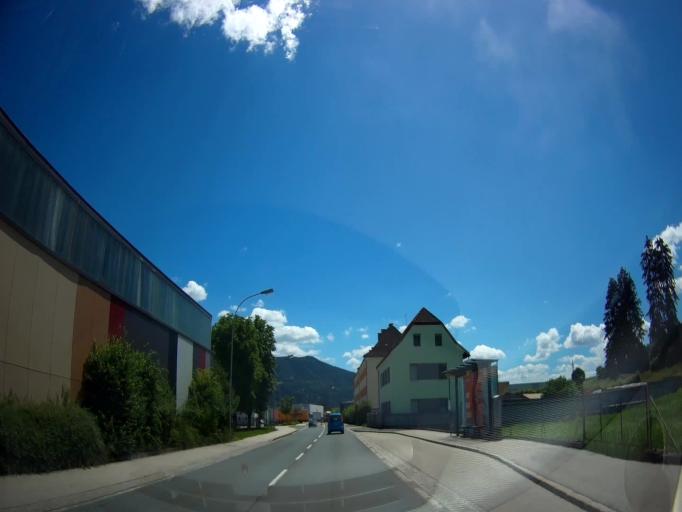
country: AT
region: Carinthia
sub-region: Politischer Bezirk Sankt Veit an der Glan
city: Sankt Veit an der Glan
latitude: 46.7559
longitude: 14.3780
